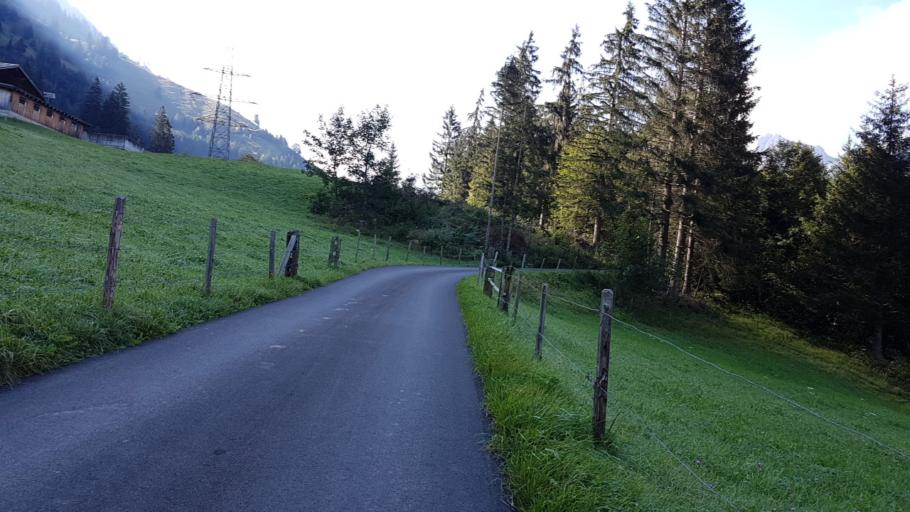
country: CH
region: Bern
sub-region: Frutigen-Niedersimmental District
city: Frutigen
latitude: 46.5544
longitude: 7.6710
